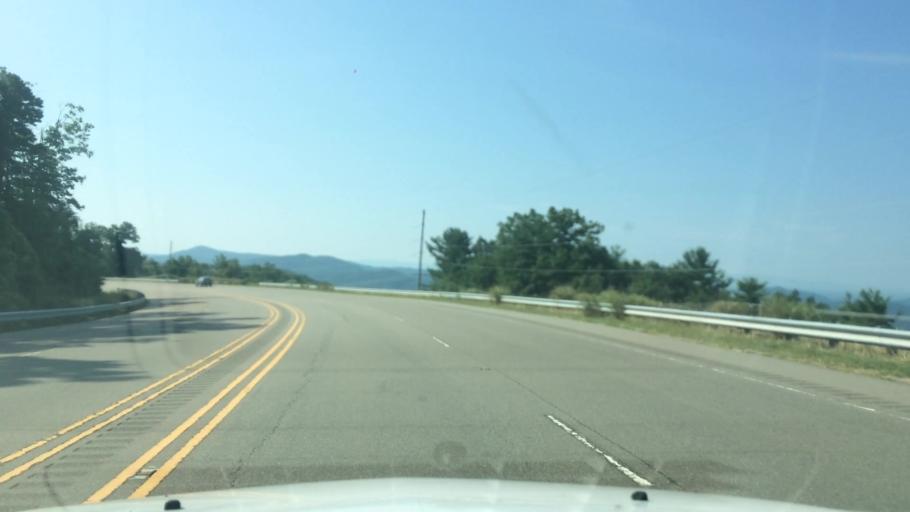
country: US
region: North Carolina
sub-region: Watauga County
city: Blowing Rock
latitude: 36.0883
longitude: -81.6343
